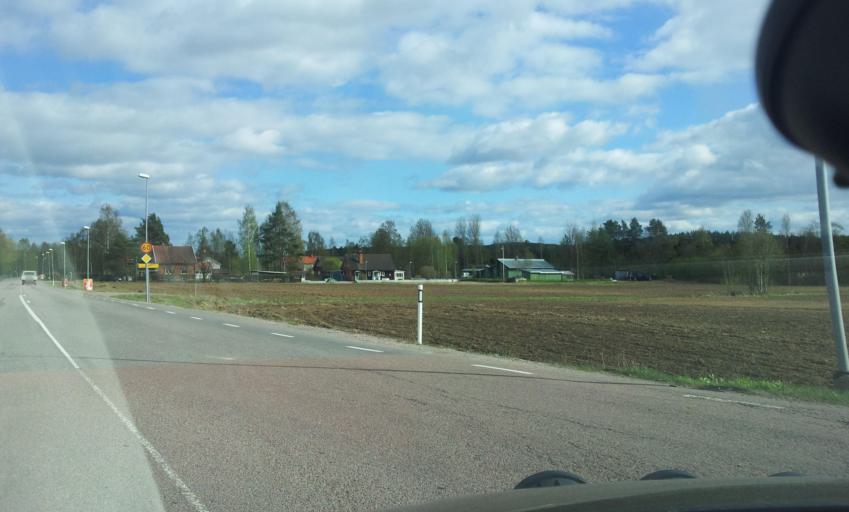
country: SE
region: Gaevleborg
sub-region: Ljusdals Kommun
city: Ljusdal
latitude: 61.8256
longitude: 16.0700
